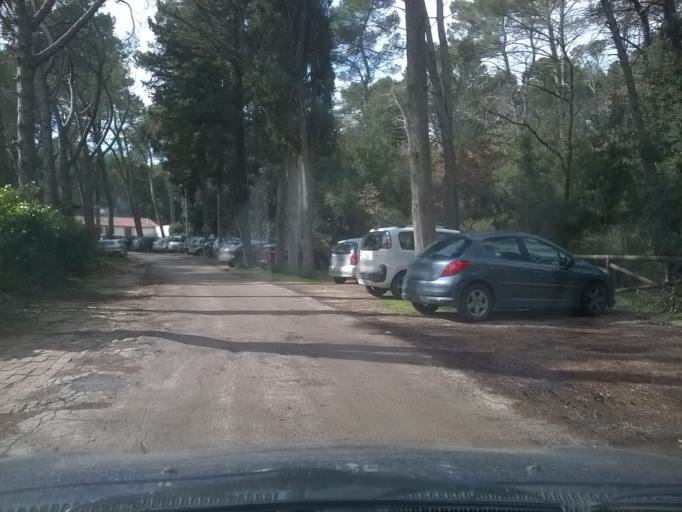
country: IT
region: Apulia
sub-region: Provincia di Bari
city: Cassano delle Murge
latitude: 40.8917
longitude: 16.6996
